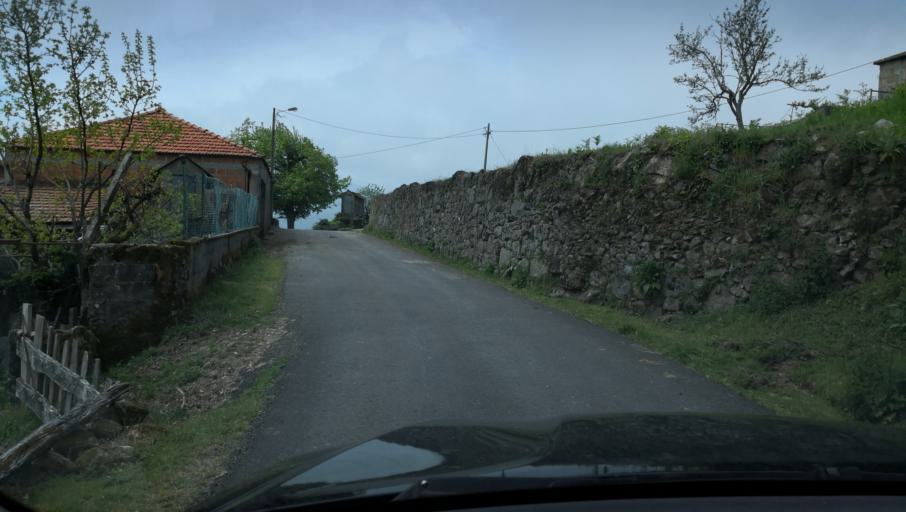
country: PT
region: Vila Real
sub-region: Vila Real
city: Vila Real
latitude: 41.2976
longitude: -7.8308
